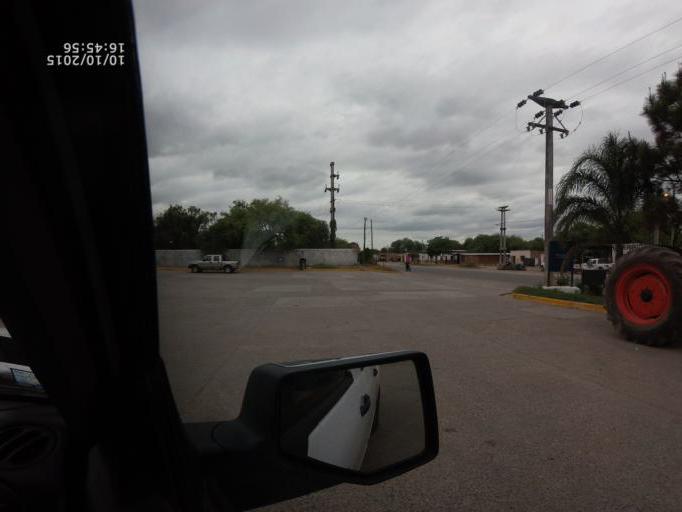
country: AR
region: Salta
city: Joaquin V. Gonzalez
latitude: -25.1238
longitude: -64.1231
